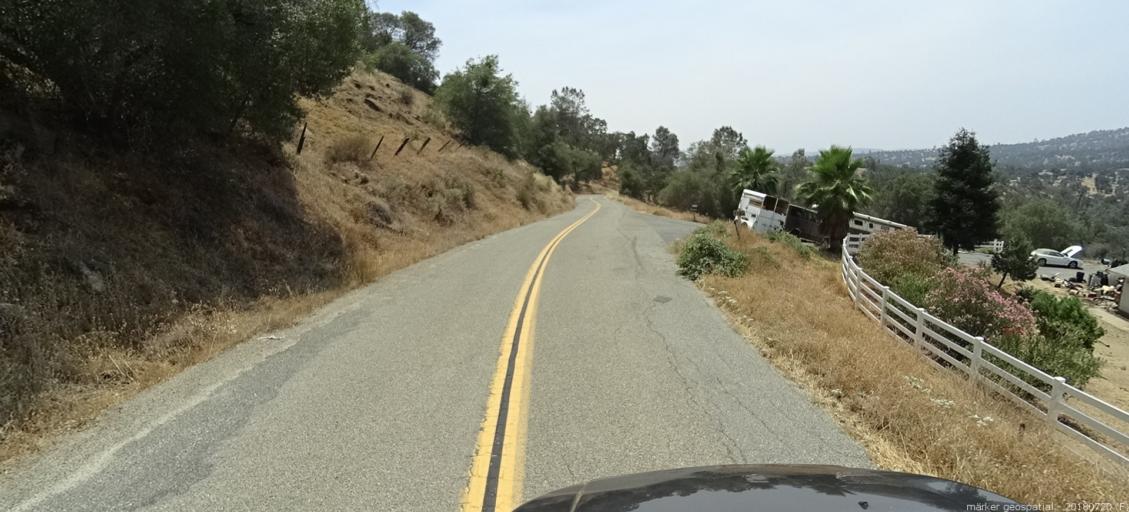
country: US
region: California
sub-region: Madera County
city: Ahwahnee
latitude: 37.2996
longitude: -119.7945
